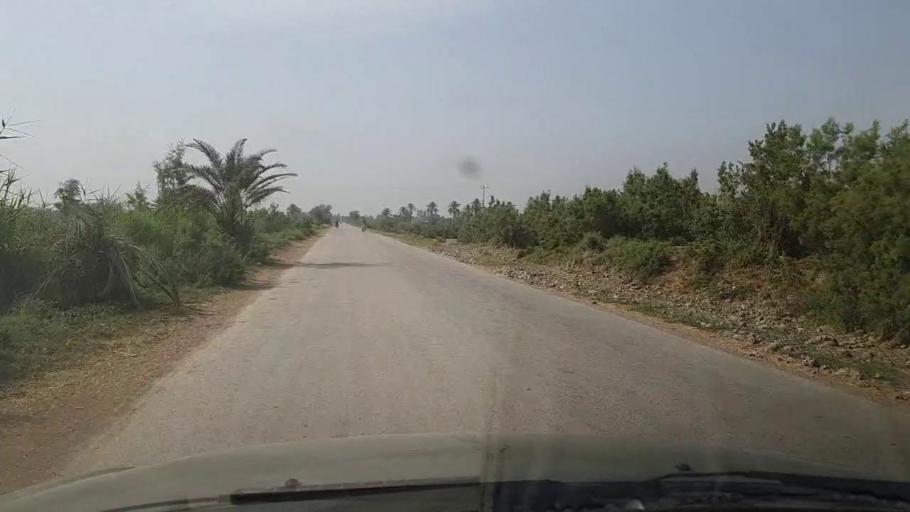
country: PK
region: Sindh
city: Gambat
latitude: 27.4485
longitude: 68.4861
